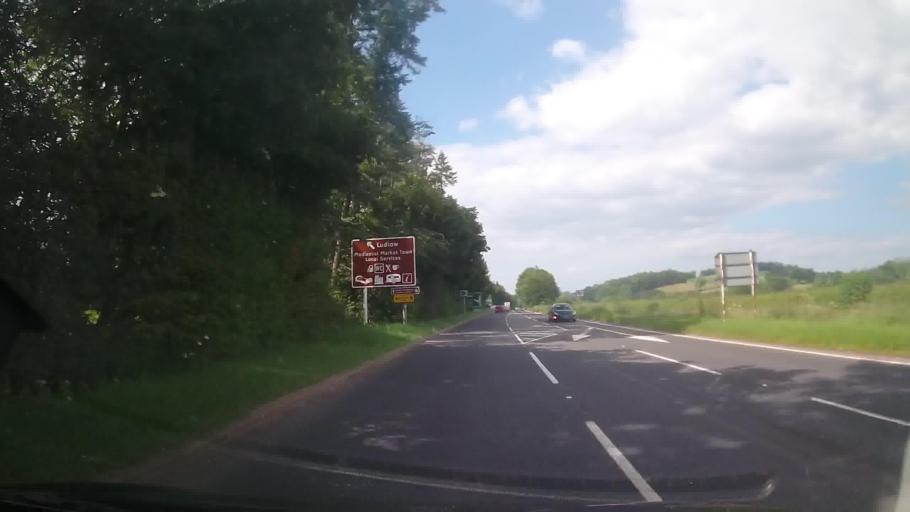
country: GB
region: England
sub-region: Shropshire
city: Ludlow
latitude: 52.3358
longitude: -2.7124
